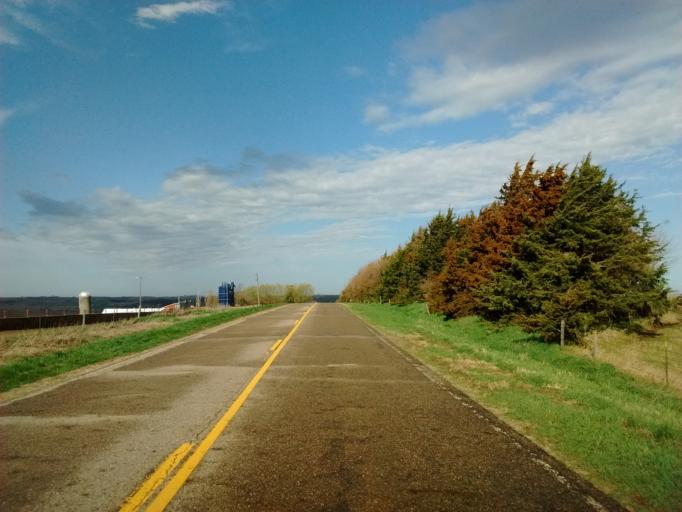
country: US
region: Iowa
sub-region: Woodbury County
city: Moville
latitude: 42.3860
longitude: -96.0492
